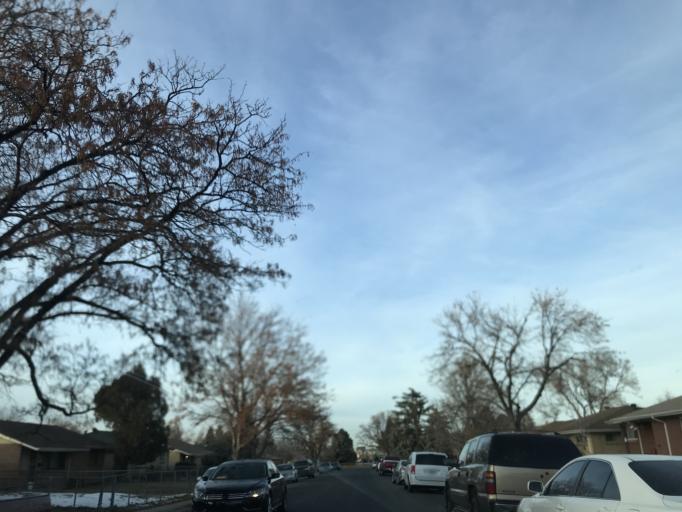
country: US
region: Colorado
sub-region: Adams County
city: Aurora
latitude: 39.7496
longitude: -104.8658
